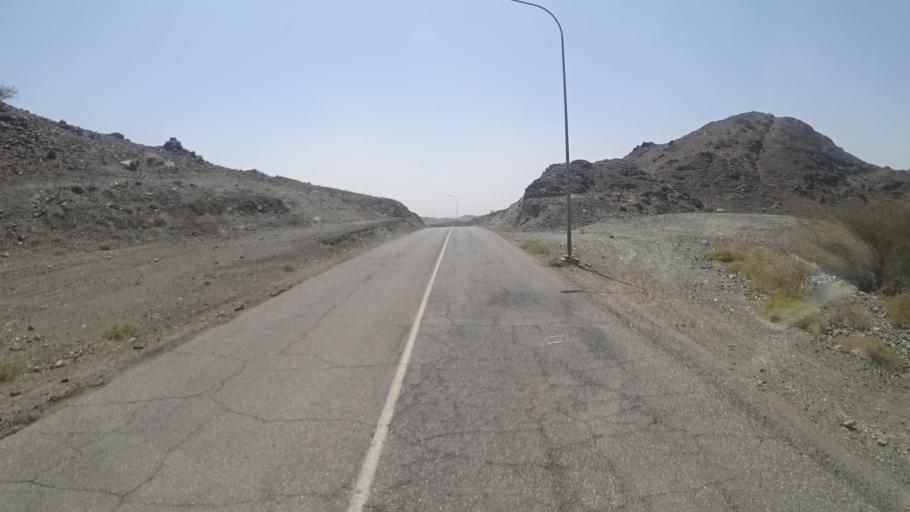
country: OM
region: Ash Sharqiyah
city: Ibra'
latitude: 22.6659
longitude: 58.5297
